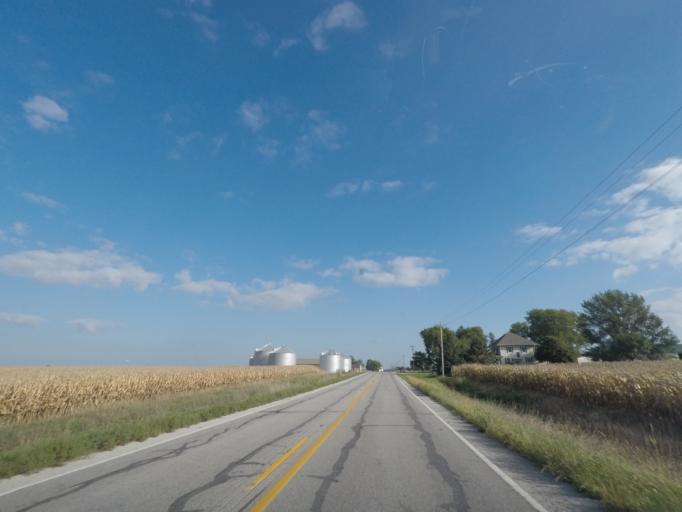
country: US
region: Iowa
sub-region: Story County
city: Nevada
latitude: 41.9963
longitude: -93.4629
